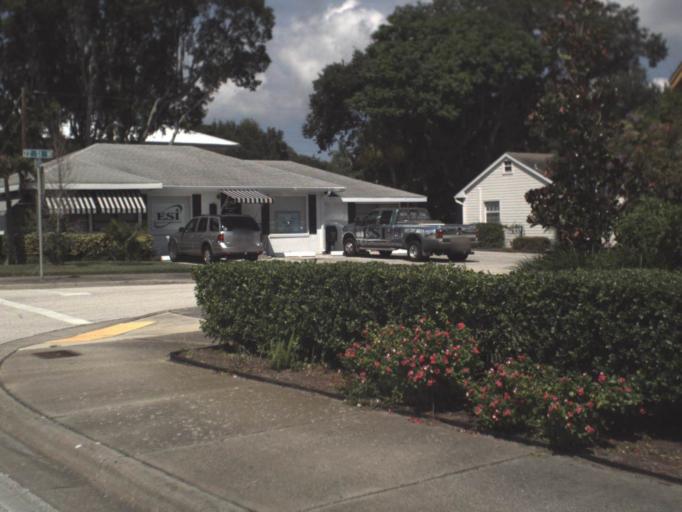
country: US
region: Florida
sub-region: Manatee County
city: Bradenton
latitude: 27.4956
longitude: -82.5836
